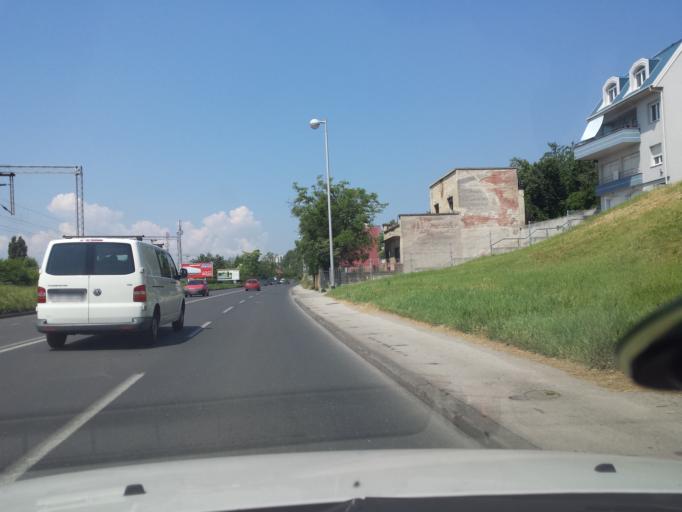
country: HR
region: Grad Zagreb
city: Jankomir
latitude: 45.8116
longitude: 15.9134
